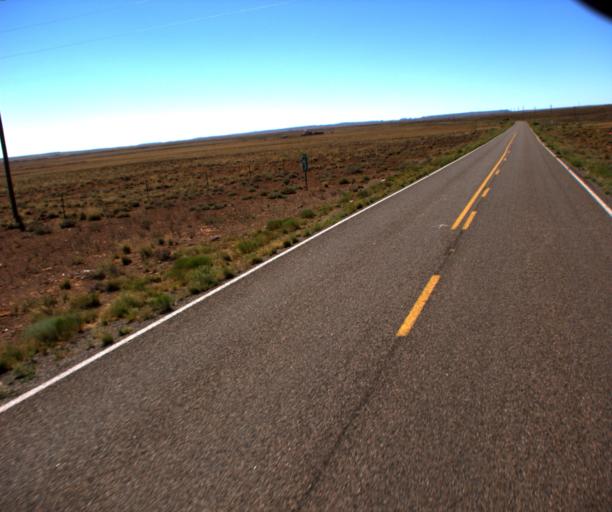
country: US
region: Arizona
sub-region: Coconino County
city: LeChee
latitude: 35.1809
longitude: -110.9294
